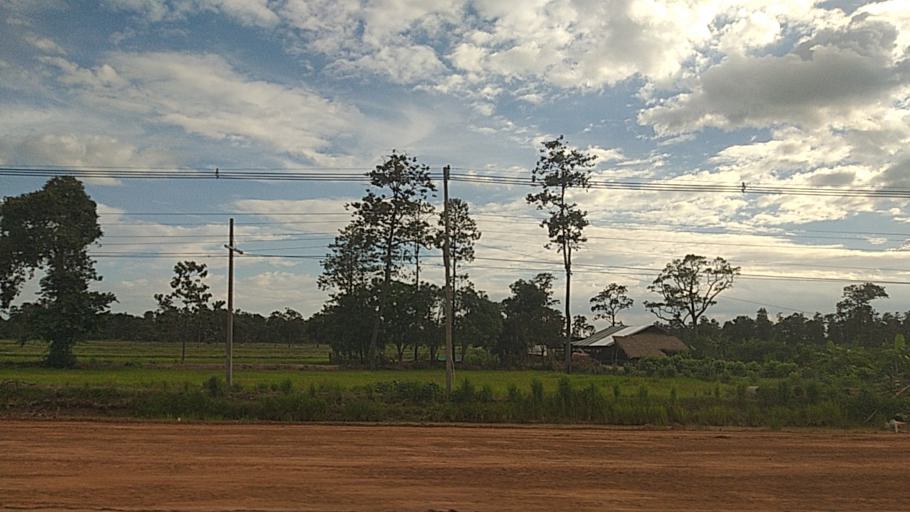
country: TH
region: Surin
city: Kap Choeng
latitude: 14.5179
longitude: 103.5446
